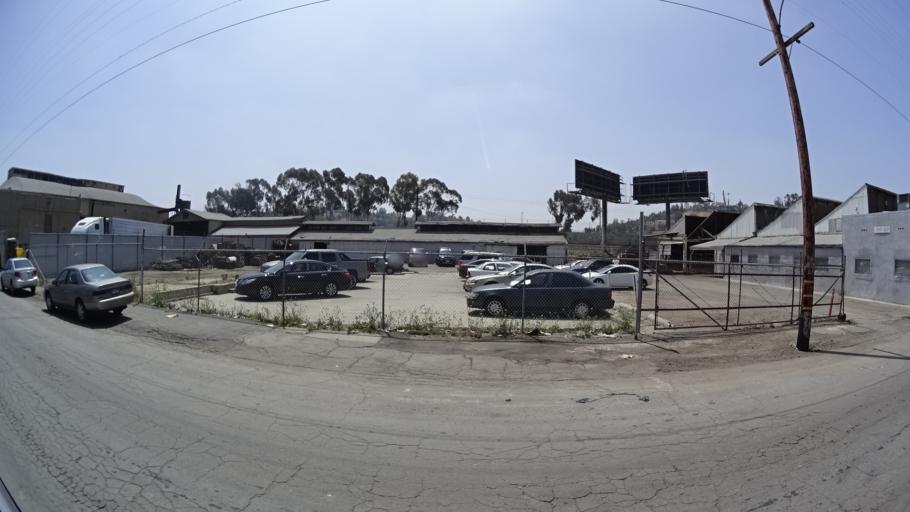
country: US
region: California
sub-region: Los Angeles County
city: Belvedere
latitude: 34.0587
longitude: -118.1804
